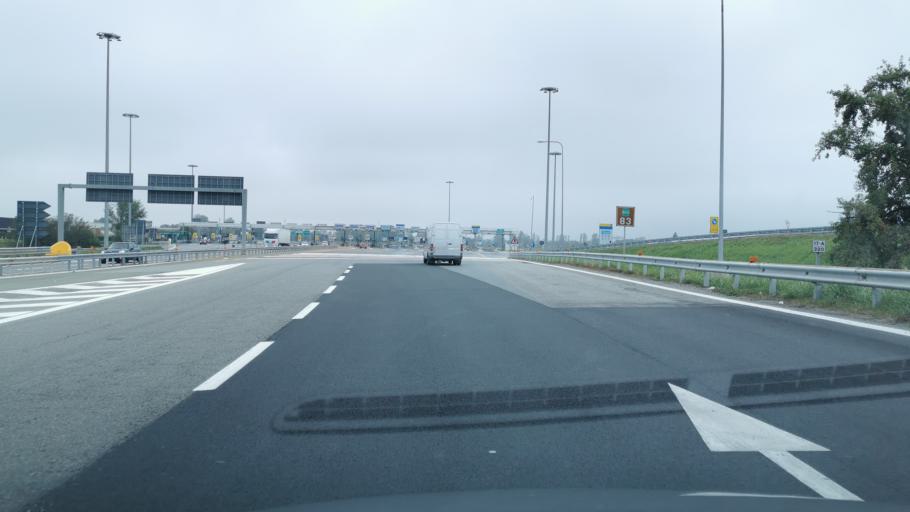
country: IT
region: Piedmont
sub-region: Provincia di Torino
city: Leini
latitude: 45.1334
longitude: 7.7136
